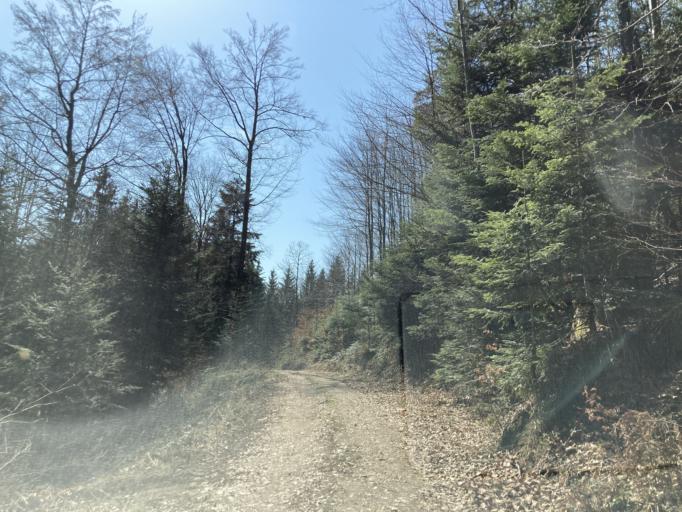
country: DE
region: Baden-Wuerttemberg
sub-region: Freiburg Region
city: Glottertal
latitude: 48.0529
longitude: 7.9809
